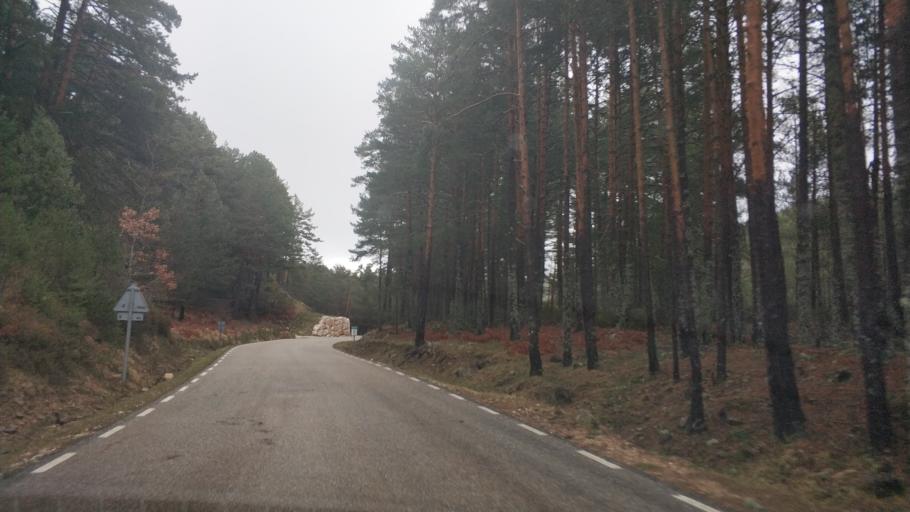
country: ES
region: Castille and Leon
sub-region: Provincia de Burgos
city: Neila
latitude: 42.0222
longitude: -3.0142
